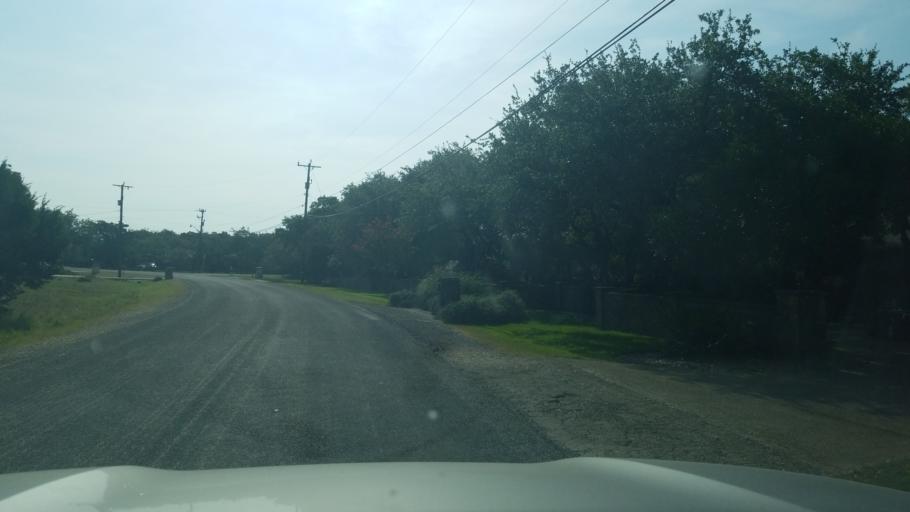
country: US
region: Texas
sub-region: Bexar County
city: Timberwood Park
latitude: 29.6997
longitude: -98.4950
